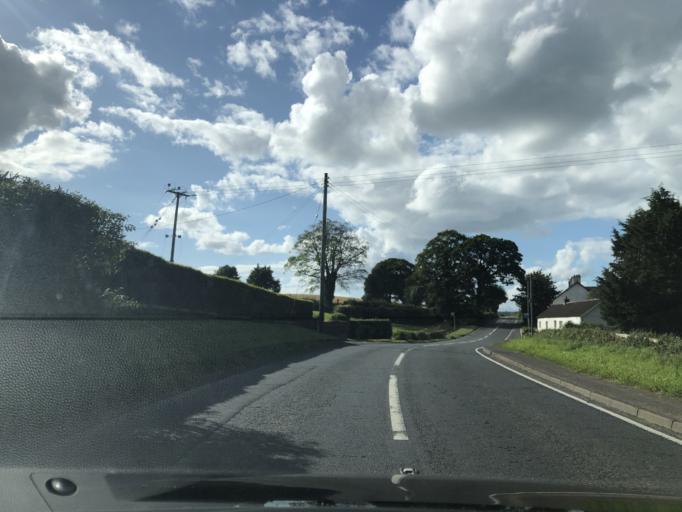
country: GB
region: Northern Ireland
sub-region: Castlereagh District
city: Dundonald
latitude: 54.5710
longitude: -5.7761
